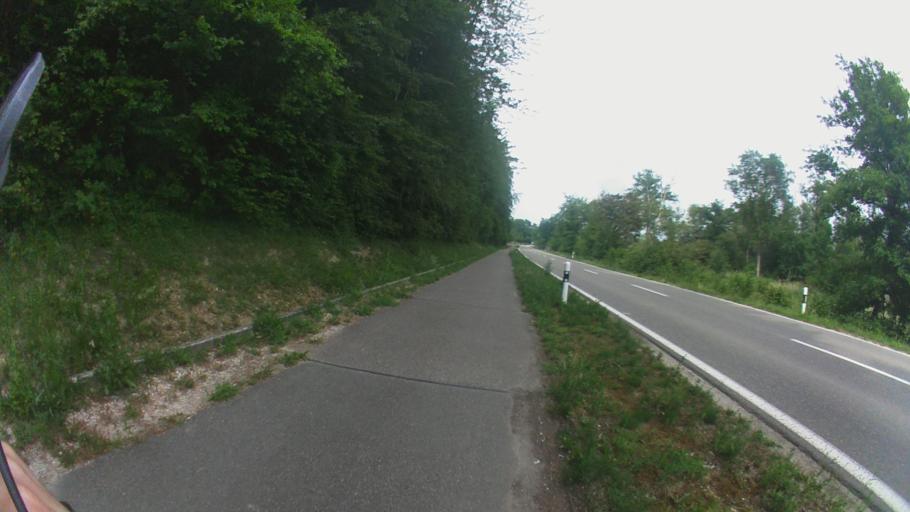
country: CH
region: Aargau
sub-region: Bezirk Zurzach
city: Koblenz
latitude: 47.5947
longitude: 8.2148
